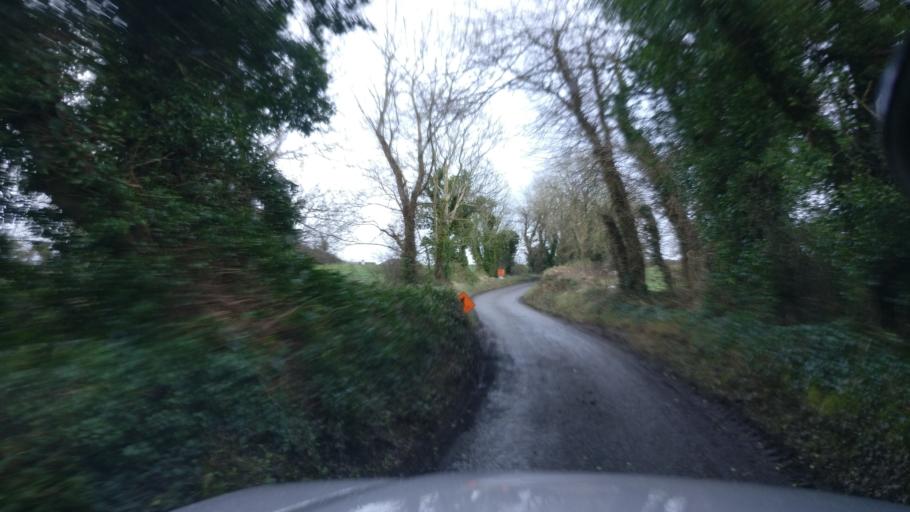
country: IE
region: Connaught
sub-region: County Galway
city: Athenry
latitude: 53.2093
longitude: -8.6883
